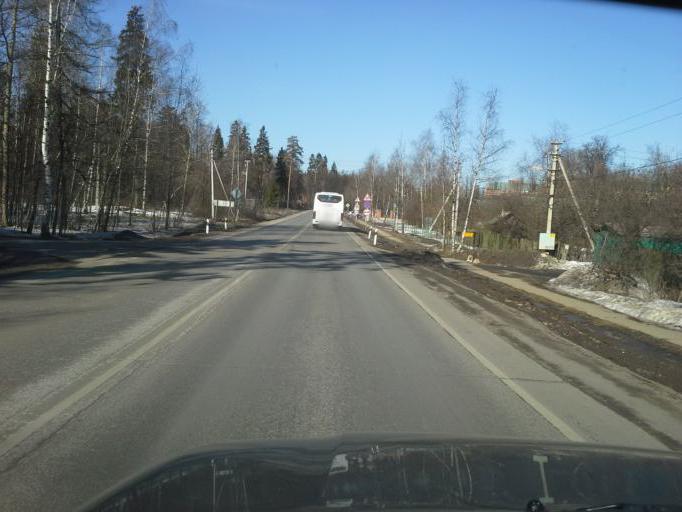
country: RU
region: Moskovskaya
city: Lesnoy Gorodok
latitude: 55.6666
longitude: 37.1765
